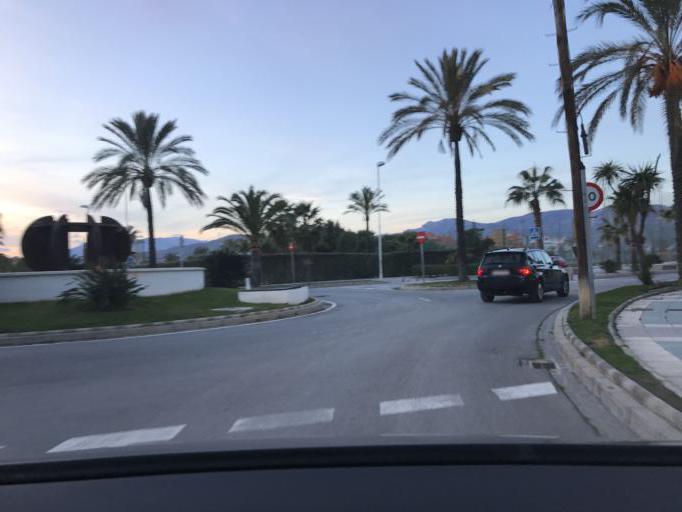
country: ES
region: Andalusia
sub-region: Provincia de Granada
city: Salobrena
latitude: 36.7199
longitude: -3.5598
